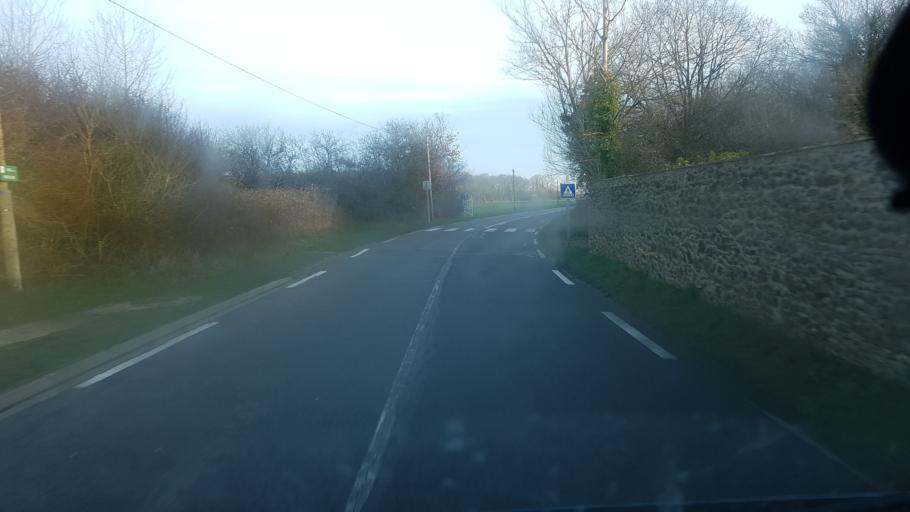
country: FR
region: Ile-de-France
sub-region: Departement des Yvelines
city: Le Perray-en-Yvelines
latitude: 48.6871
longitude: 1.8681
